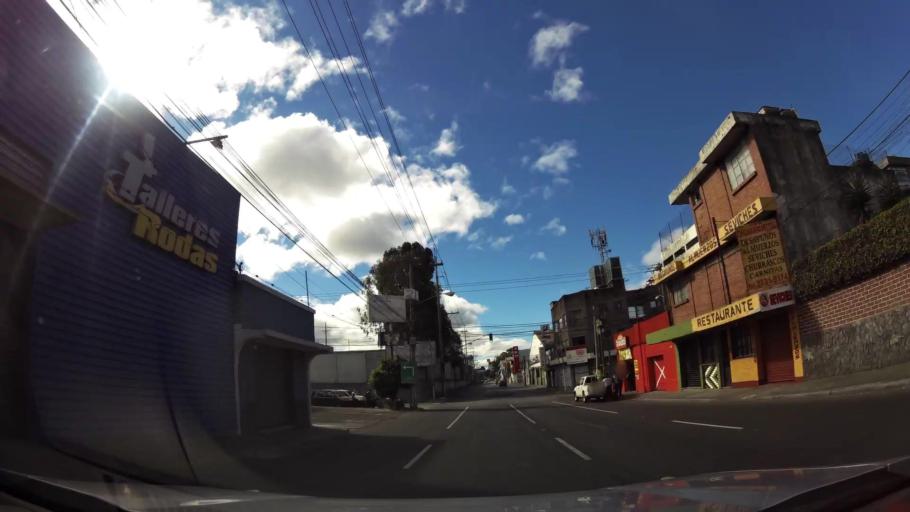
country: GT
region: Guatemala
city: Guatemala City
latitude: 14.6177
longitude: -90.5101
